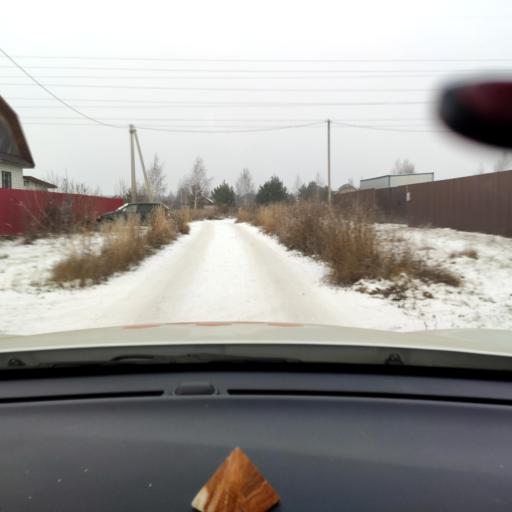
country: RU
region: Tatarstan
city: Stolbishchi
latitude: 55.7737
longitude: 49.2685
